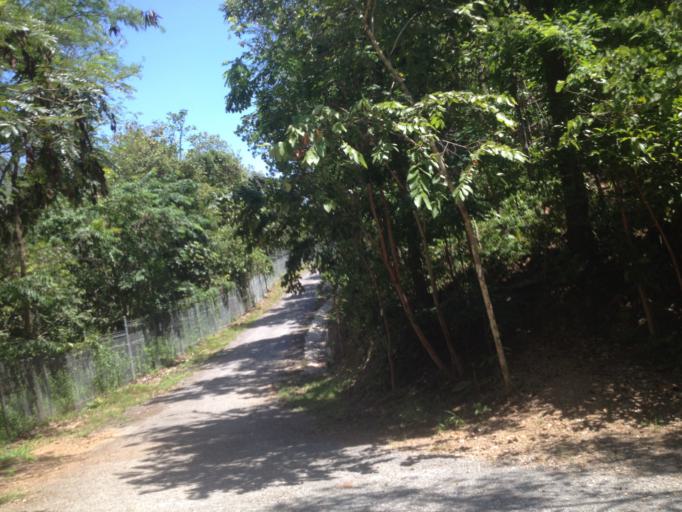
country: TH
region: Chiang Mai
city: Hang Dong
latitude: 18.7404
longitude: 98.9104
